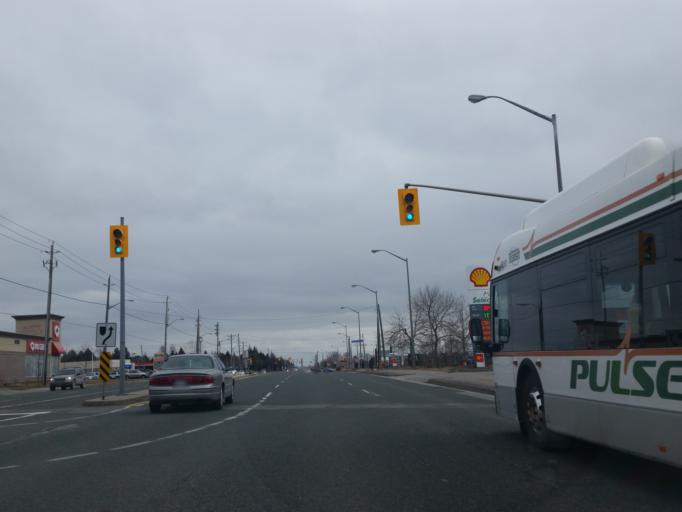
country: CA
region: Ontario
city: Pickering
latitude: 43.7970
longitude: -79.1490
